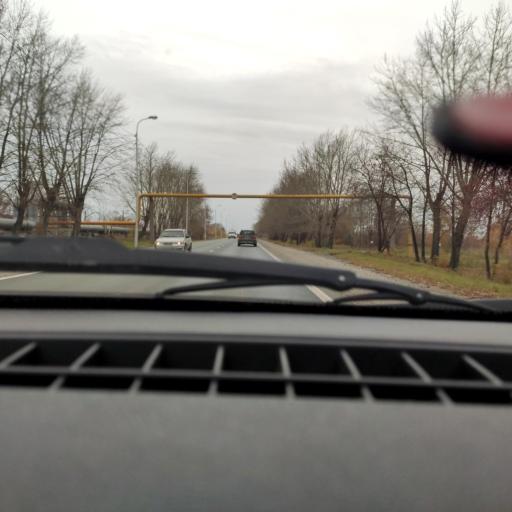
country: RU
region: Bashkortostan
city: Ufa
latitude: 54.8547
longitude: 56.1158
